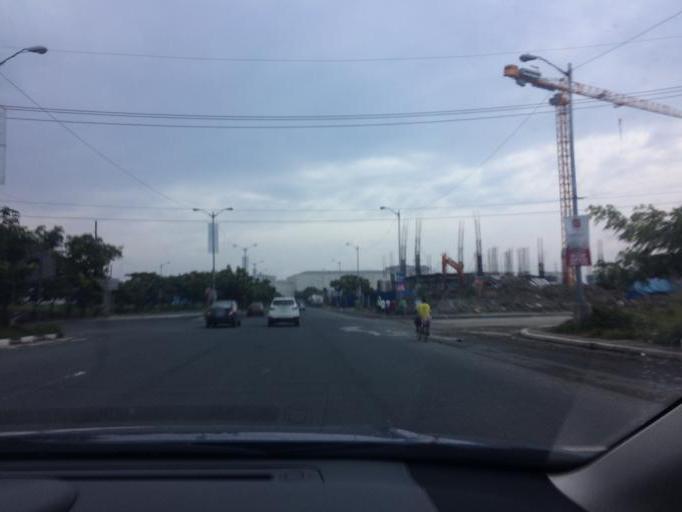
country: PH
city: Sambayanihan People's Village
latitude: 14.5105
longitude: 120.9894
